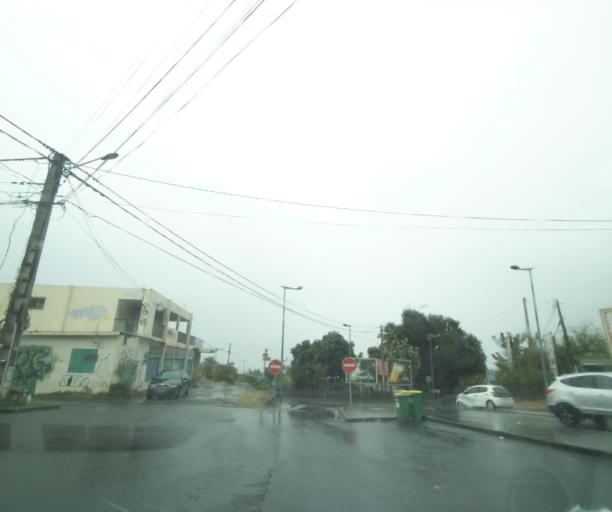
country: RE
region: Reunion
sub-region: Reunion
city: La Possession
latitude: -20.9778
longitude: 55.3288
